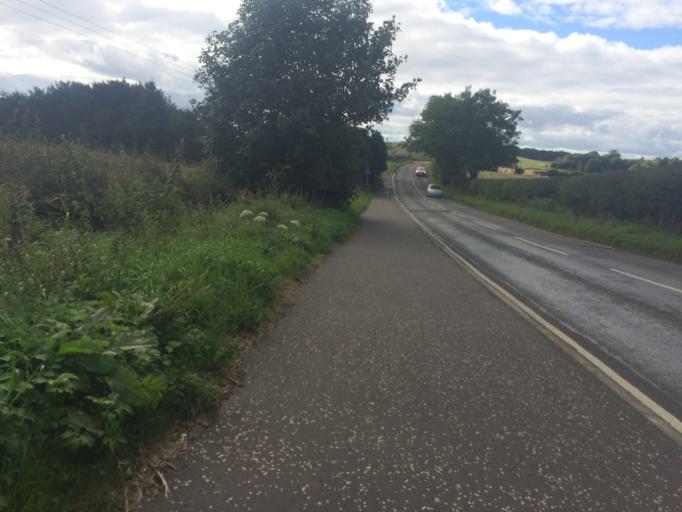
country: GB
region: Scotland
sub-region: Fife
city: Townhill
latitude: 56.0935
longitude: -3.4154
